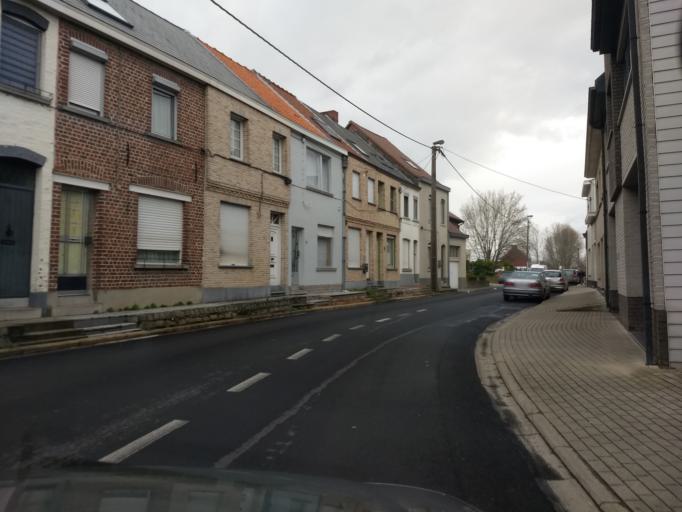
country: BE
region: Flanders
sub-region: Provincie Oost-Vlaanderen
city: Denderleeuw
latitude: 50.8585
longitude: 4.0492
